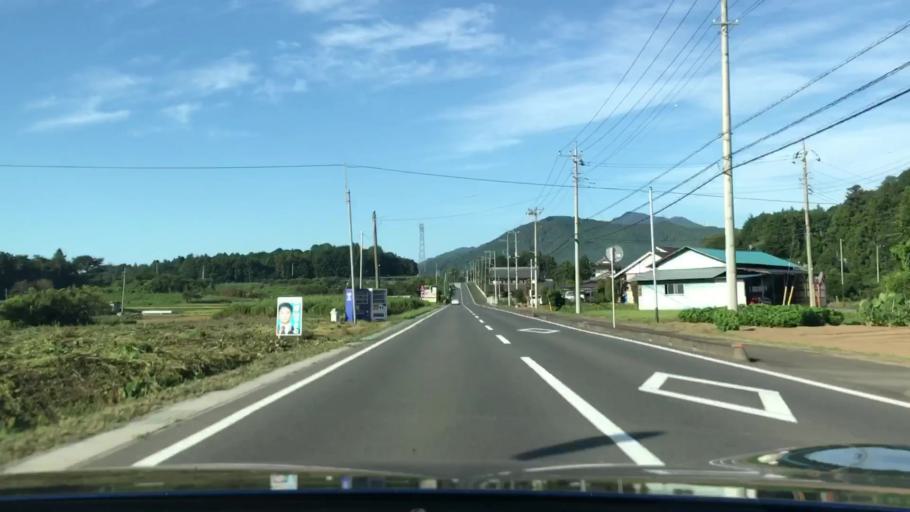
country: JP
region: Ibaraki
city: Makabe
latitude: 36.2668
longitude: 140.1792
